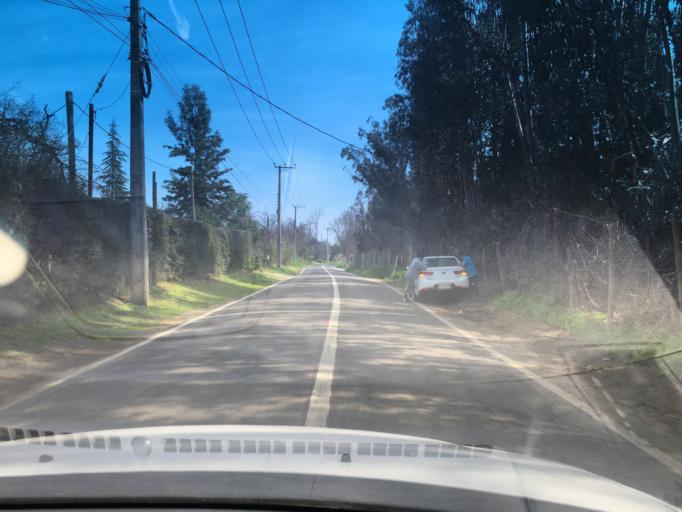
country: CL
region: Valparaiso
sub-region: Provincia de Marga Marga
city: Limache
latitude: -33.0094
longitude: -71.2190
